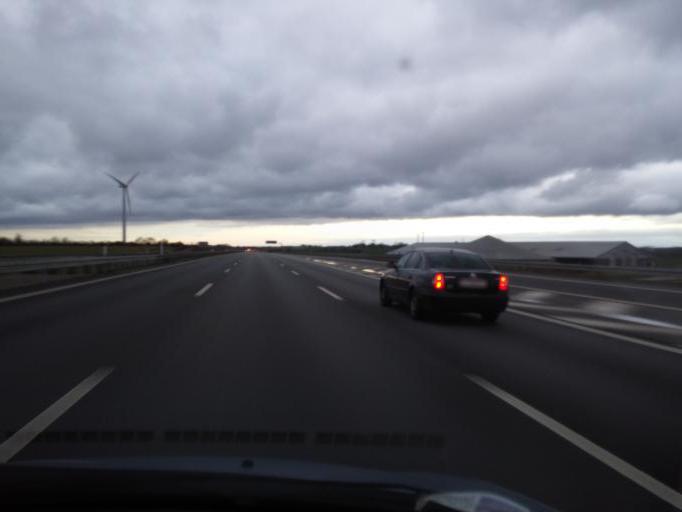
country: DK
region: South Denmark
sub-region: Middelfart Kommune
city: Norre Aby
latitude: 55.4892
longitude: 9.8366
